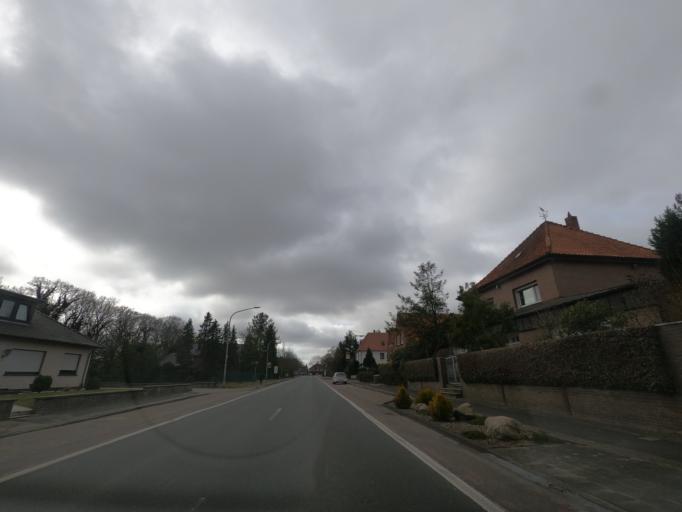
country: DE
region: Lower Saxony
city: Loningen
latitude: 52.7334
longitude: 7.7502
